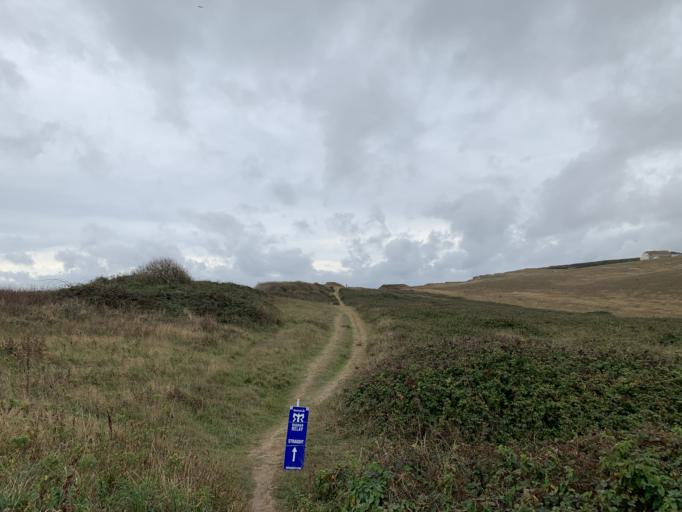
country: GB
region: England
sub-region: East Sussex
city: Newhaven
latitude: 50.7815
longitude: 0.0410
